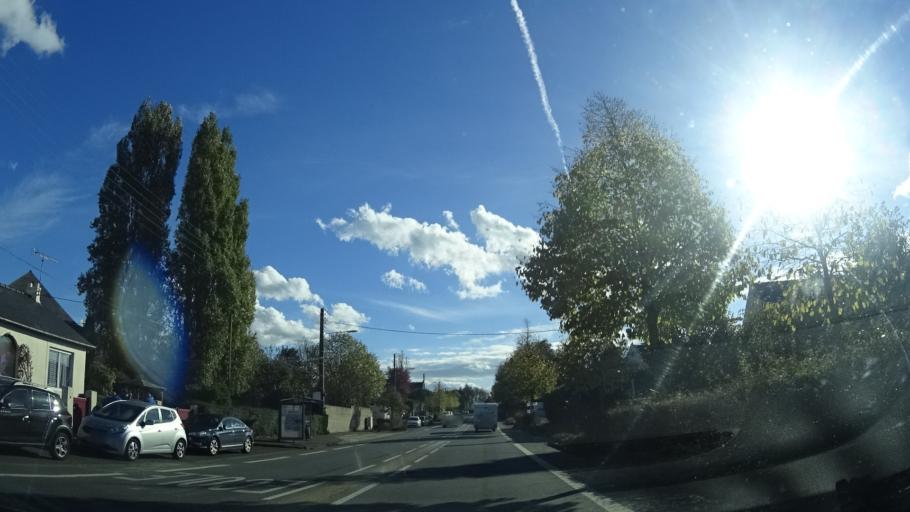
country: FR
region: Brittany
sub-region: Departement d'Ille-et-Vilaine
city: Saint-Malo
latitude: 48.6240
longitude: -2.0044
